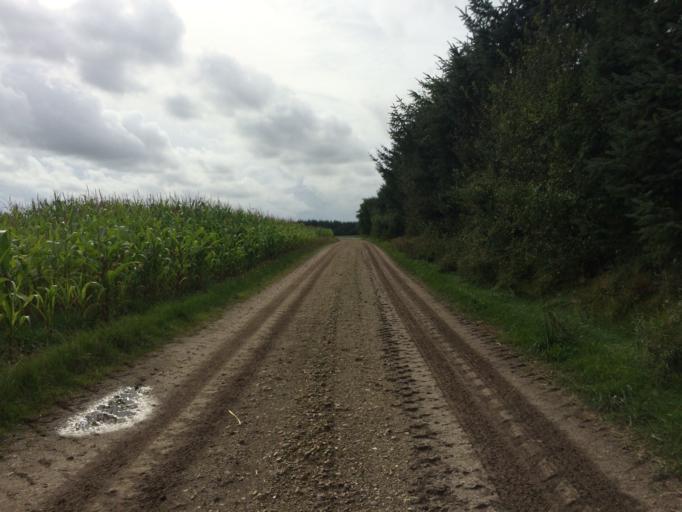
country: DK
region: Central Jutland
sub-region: Holstebro Kommune
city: Ulfborg
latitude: 56.2271
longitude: 8.3859
